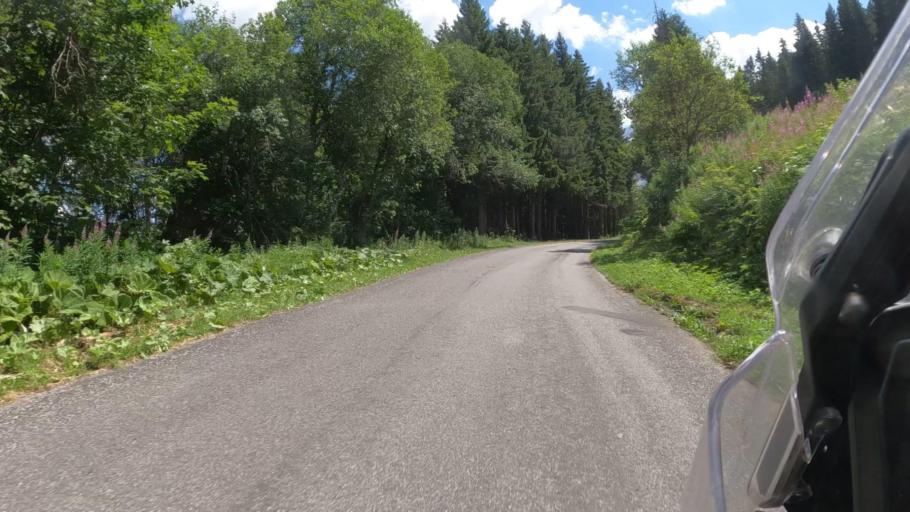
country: CH
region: Vaud
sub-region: Aigle District
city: Villars-sur-Ollon
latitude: 46.3468
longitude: 7.1447
